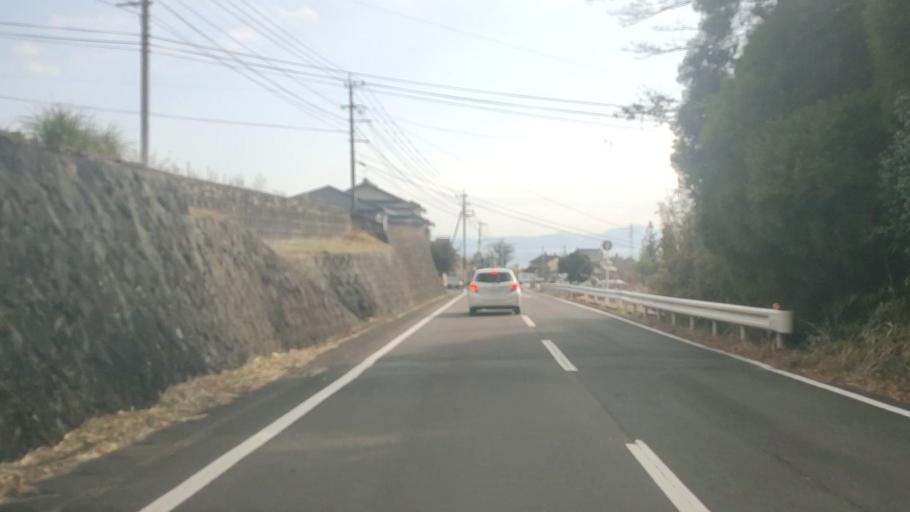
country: JP
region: Nagasaki
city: Shimabara
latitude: 32.6730
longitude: 130.2820
